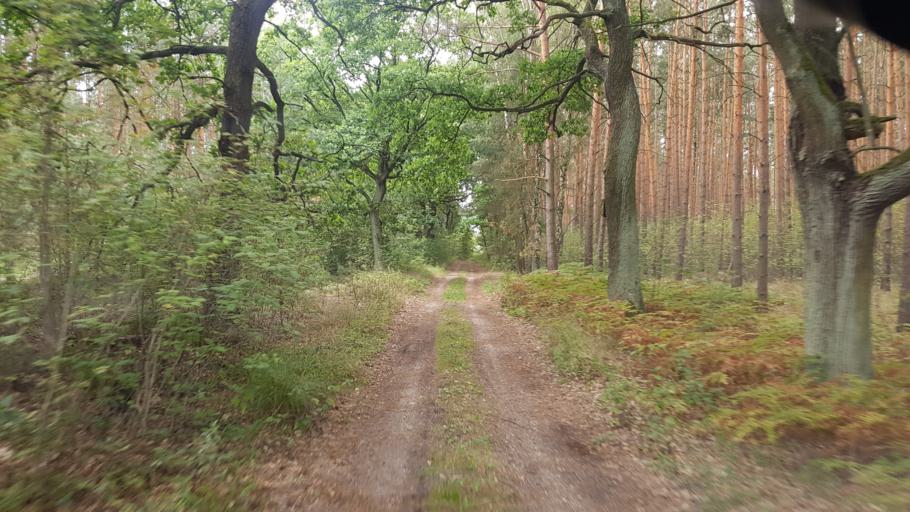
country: DE
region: Brandenburg
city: Ruckersdorf
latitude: 51.5793
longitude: 13.6006
